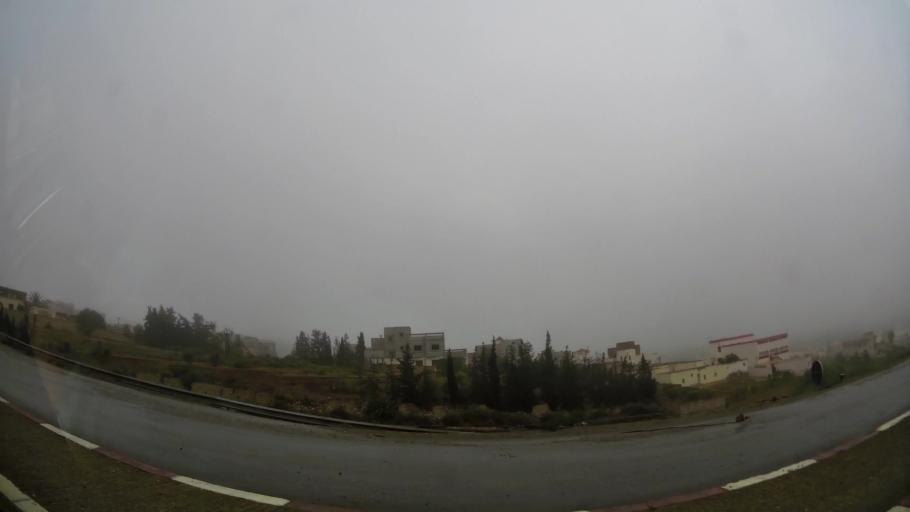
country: MA
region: Taza-Al Hoceima-Taounate
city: Imzourene
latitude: 35.1977
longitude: -3.9020
